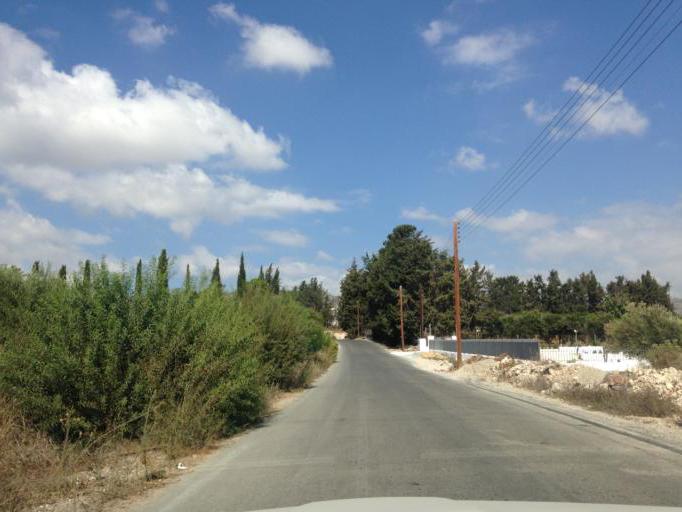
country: CY
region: Pafos
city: Pegeia
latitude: 34.8670
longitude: 32.3614
